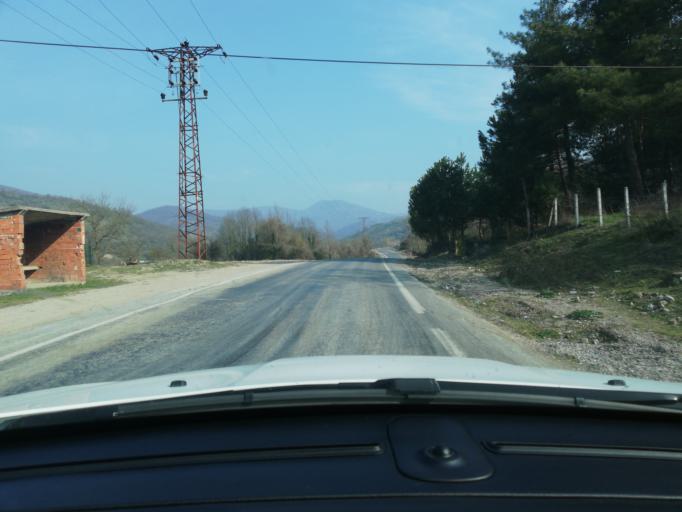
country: TR
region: Karabuk
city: Yenice
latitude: 41.2299
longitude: 32.3607
